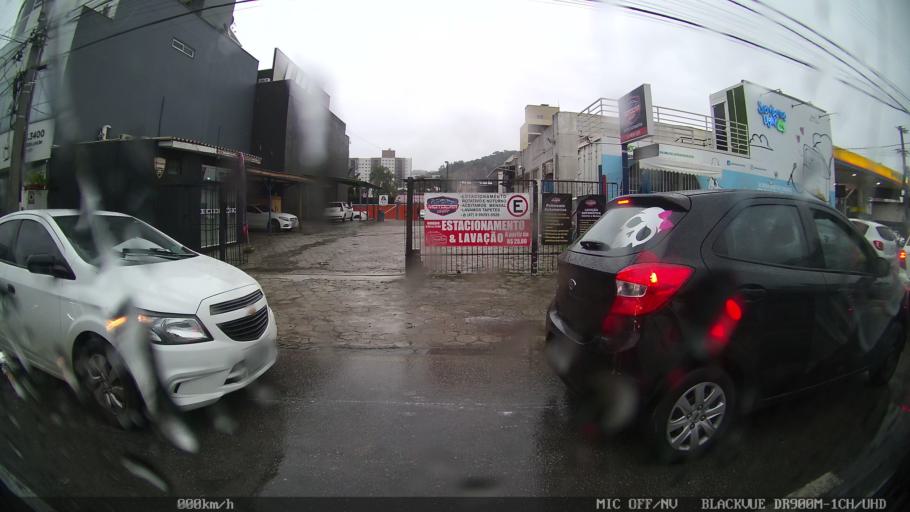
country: BR
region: Santa Catarina
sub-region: Balneario Camboriu
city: Balneario Camboriu
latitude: -26.9945
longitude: -48.6417
